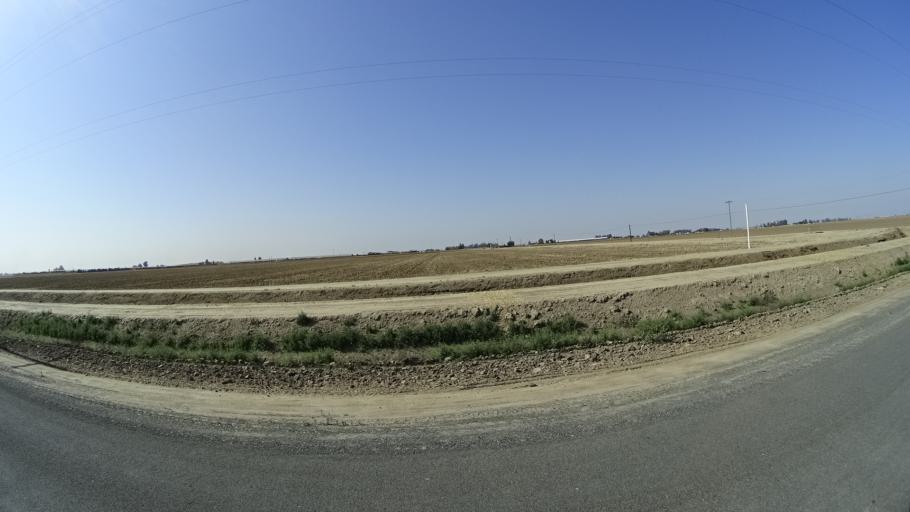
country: US
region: California
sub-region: Kings County
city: Home Garden
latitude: 36.2404
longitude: -119.6179
